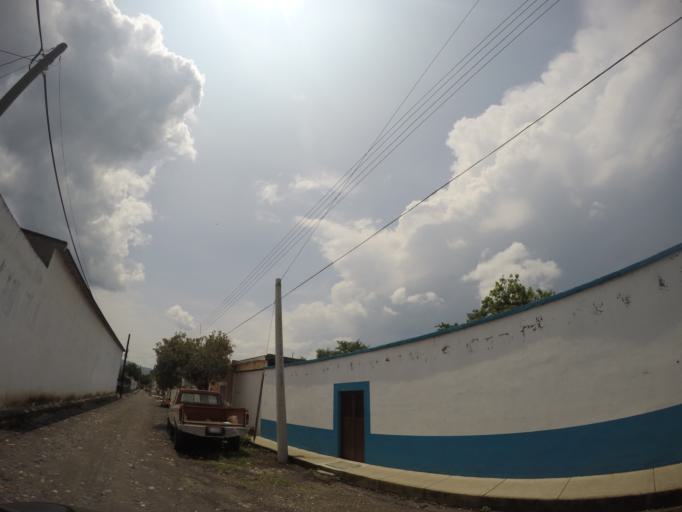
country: MX
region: Nayarit
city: Jala
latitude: 21.1074
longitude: -104.4423
